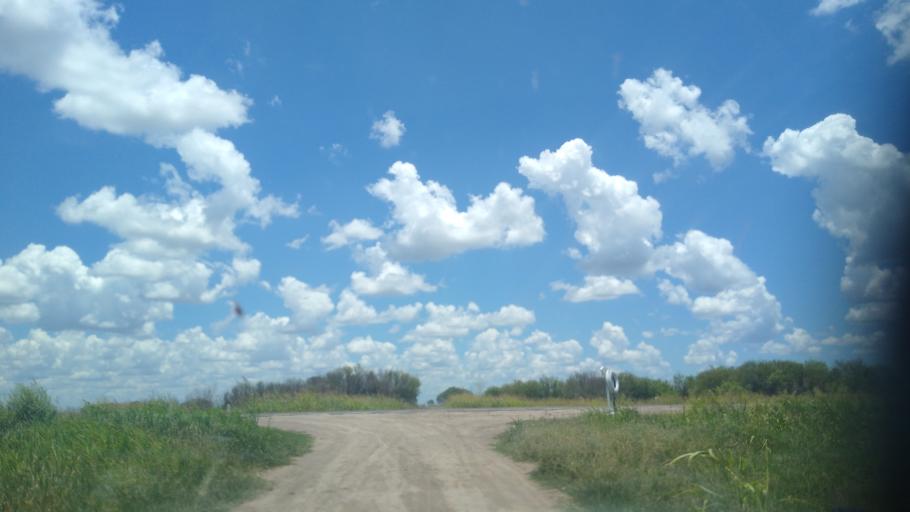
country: AR
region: Chaco
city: Presidencia Roque Saenz Pena
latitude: -26.7321
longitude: -60.3827
